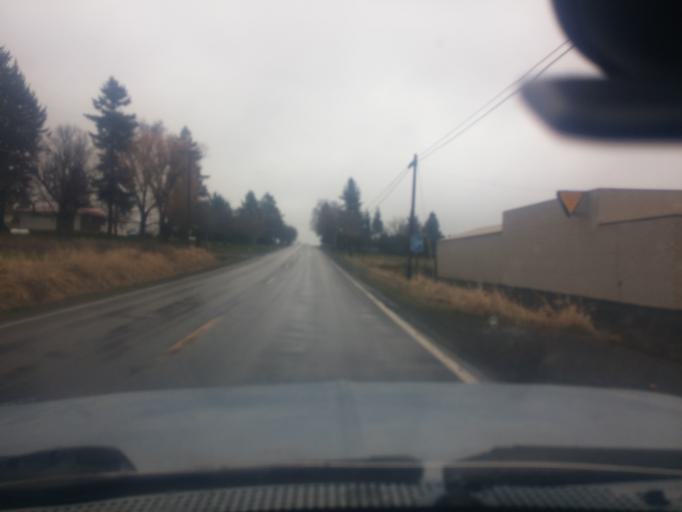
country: US
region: Idaho
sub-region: Latah County
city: Moscow
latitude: 46.9142
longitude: -116.8502
